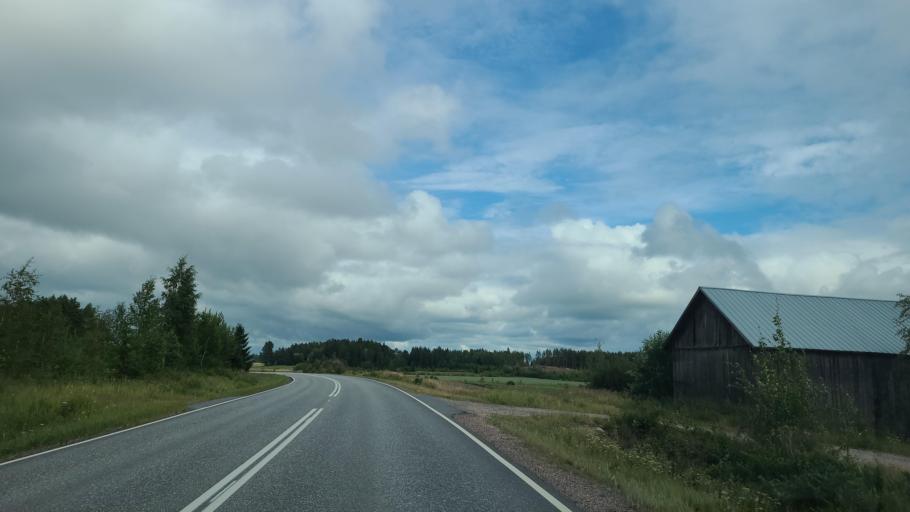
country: FI
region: Varsinais-Suomi
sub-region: Aboland-Turunmaa
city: Dragsfjaerd
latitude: 60.1030
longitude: 22.5859
